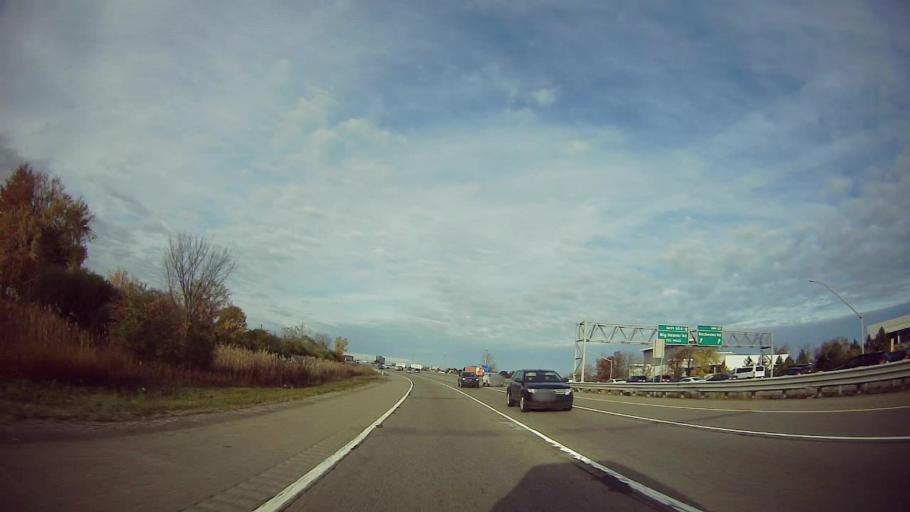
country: US
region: Michigan
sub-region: Oakland County
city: Clawson
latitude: 42.5591
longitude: -83.1235
